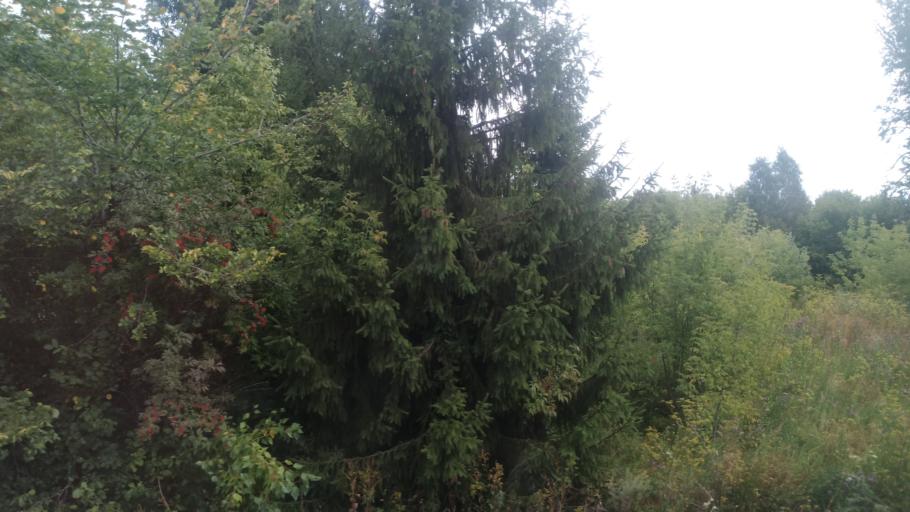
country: RU
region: Altai Krai
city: Nalobikha
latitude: 53.2492
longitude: 84.4426
